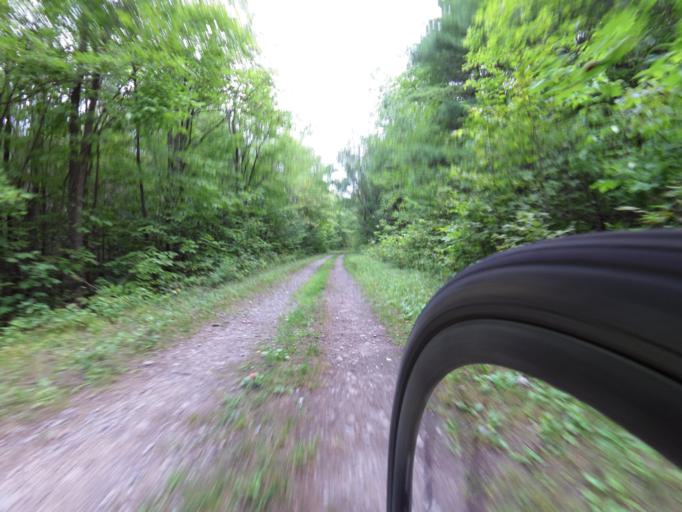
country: CA
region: Ontario
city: Gananoque
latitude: 44.5880
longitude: -76.3091
